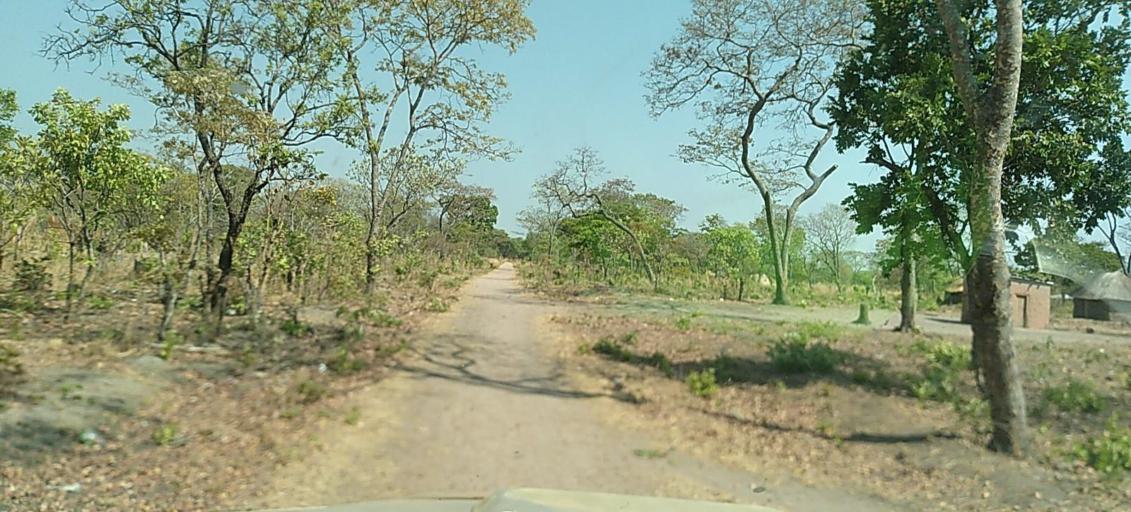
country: ZM
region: North-Western
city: Kalengwa
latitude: -13.3070
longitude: 24.8043
